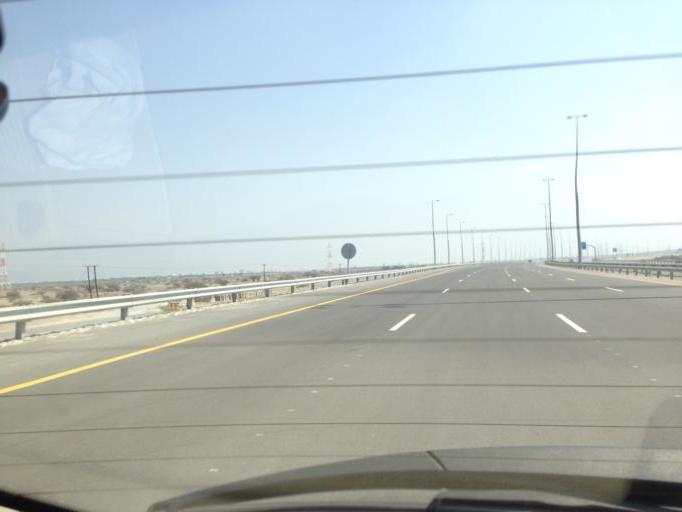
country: OM
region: Al Batinah
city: Barka'
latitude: 23.6307
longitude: 57.8543
